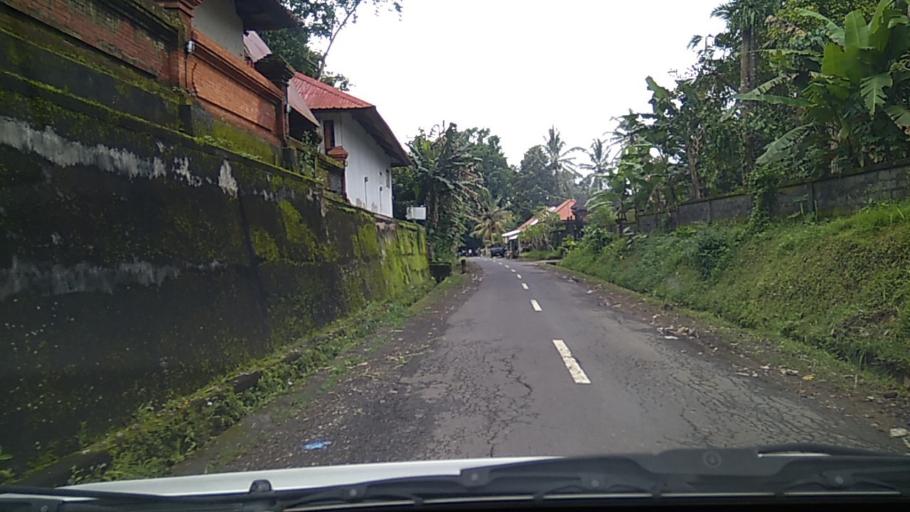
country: ID
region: Bali
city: Brahmana
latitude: -8.4774
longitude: 115.2012
